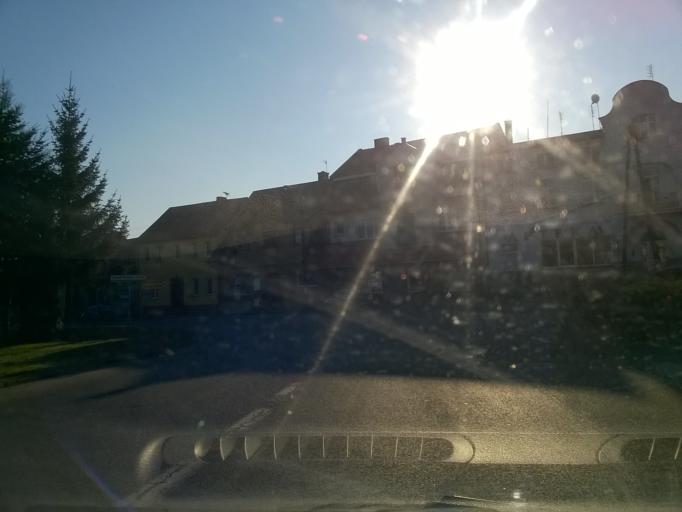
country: PL
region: Greater Poland Voivodeship
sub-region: Powiat wagrowiecki
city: Golancz
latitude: 52.9440
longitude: 17.2998
